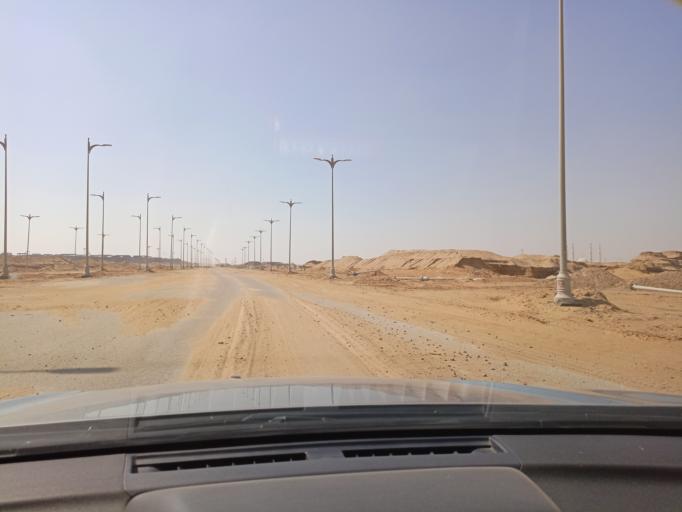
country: EG
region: Muhafazat al Qalyubiyah
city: Al Khankah
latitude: 30.0092
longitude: 31.6147
